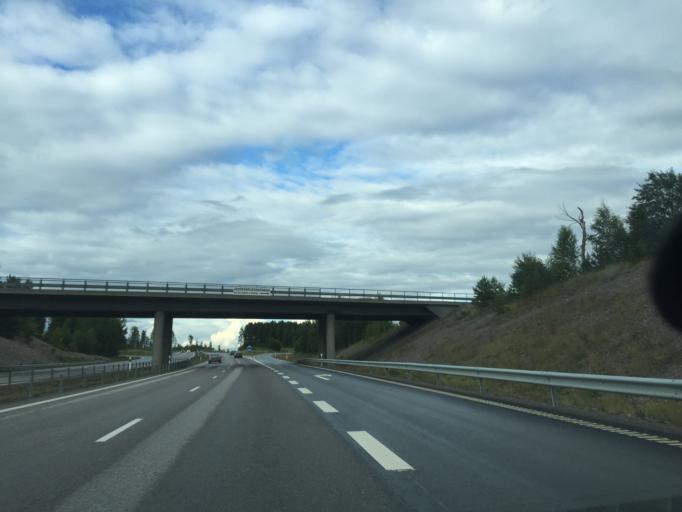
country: SE
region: Vaestmanland
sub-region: Arboga Kommun
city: Arboga
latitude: 59.4118
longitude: 15.7682
